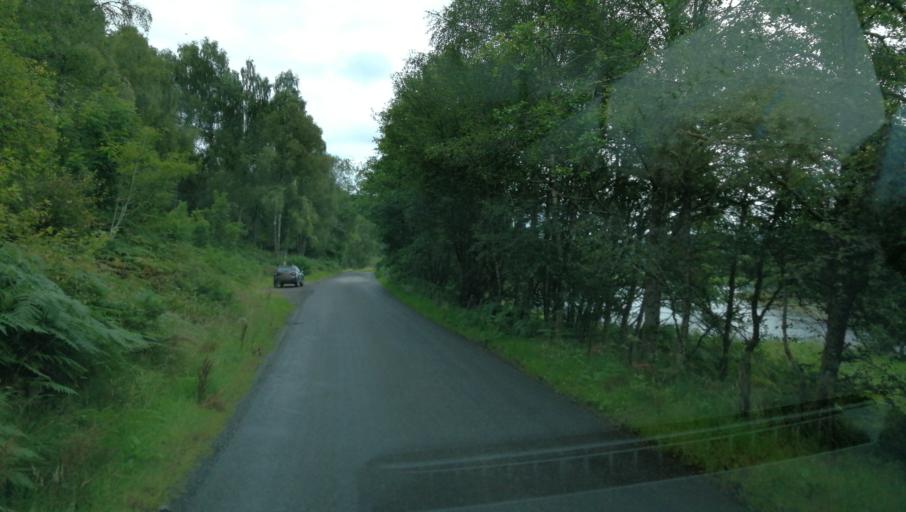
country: GB
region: Scotland
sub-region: Highland
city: Beauly
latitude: 57.3388
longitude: -4.7780
